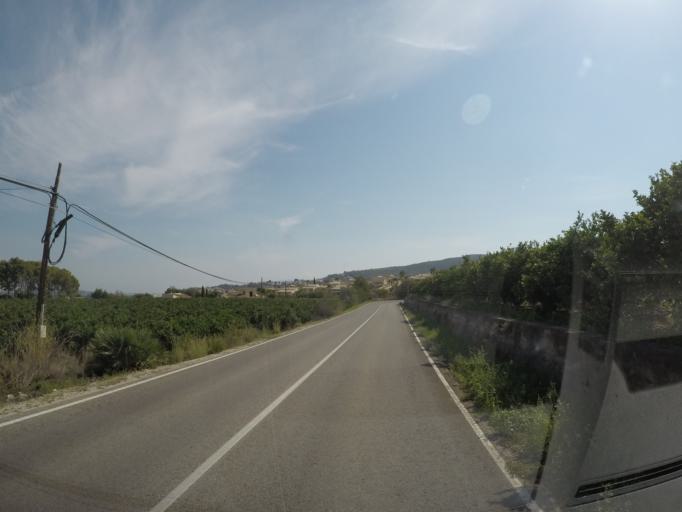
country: ES
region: Valencia
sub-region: Provincia de Alicante
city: Orba
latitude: 38.7815
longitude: -0.0751
